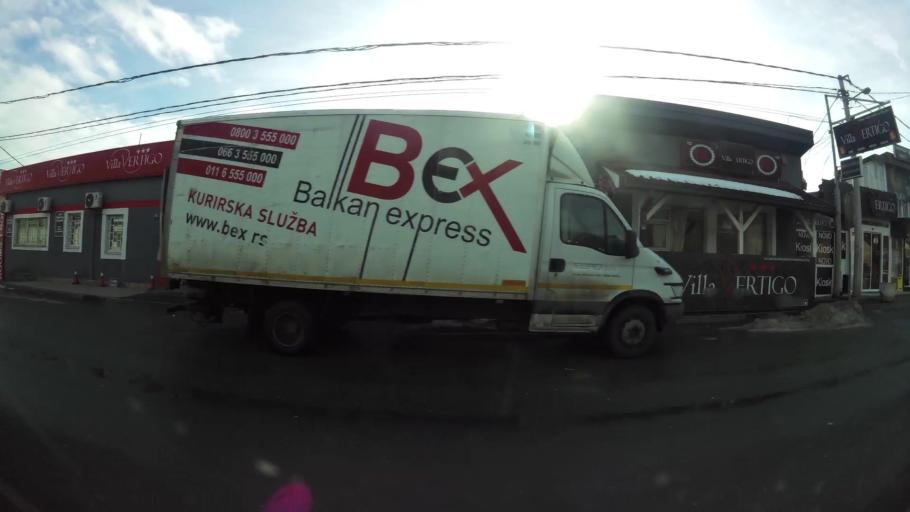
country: RS
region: Central Serbia
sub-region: Belgrade
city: Rakovica
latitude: 44.7174
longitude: 20.4242
